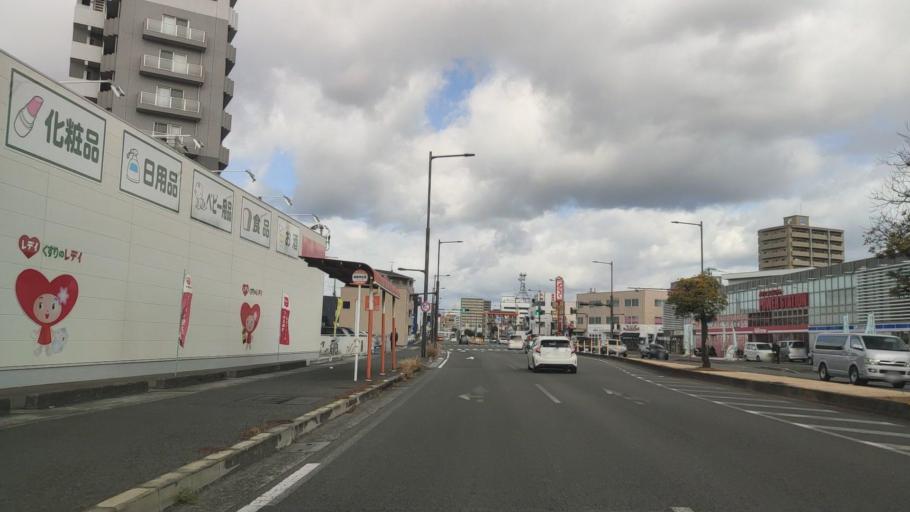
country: JP
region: Ehime
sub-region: Shikoku-chuo Shi
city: Matsuyama
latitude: 33.8271
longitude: 132.7588
